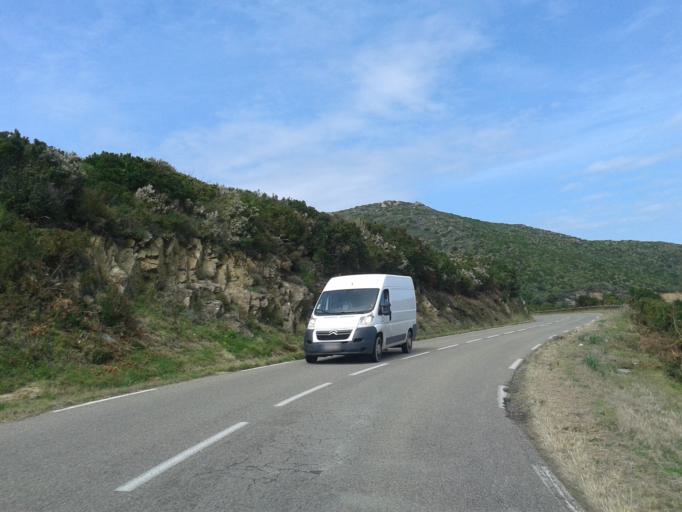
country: FR
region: Corsica
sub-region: Departement de la Haute-Corse
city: Brando
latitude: 42.8461
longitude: 9.4830
